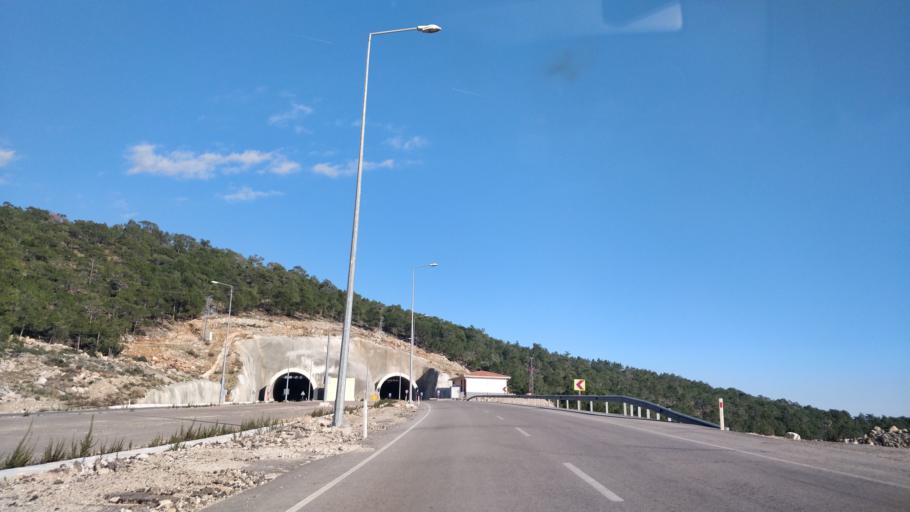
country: TR
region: Mersin
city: Ovacik
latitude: 36.1655
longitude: 33.5750
